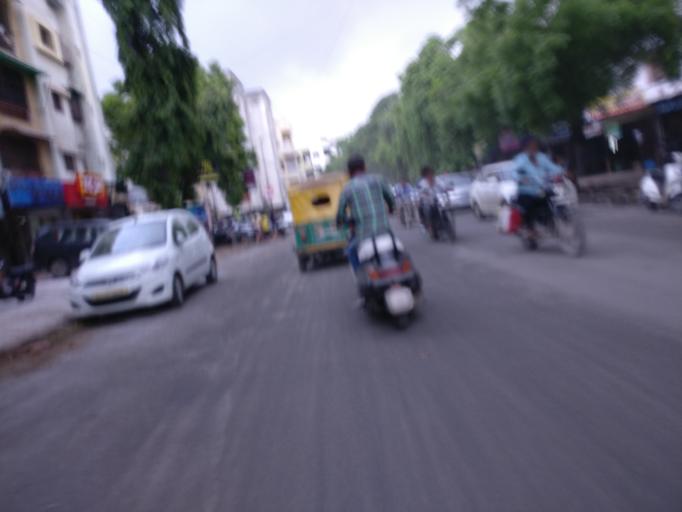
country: IN
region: Gujarat
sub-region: Ahmadabad
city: Ahmedabad
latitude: 23.0098
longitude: 72.5598
